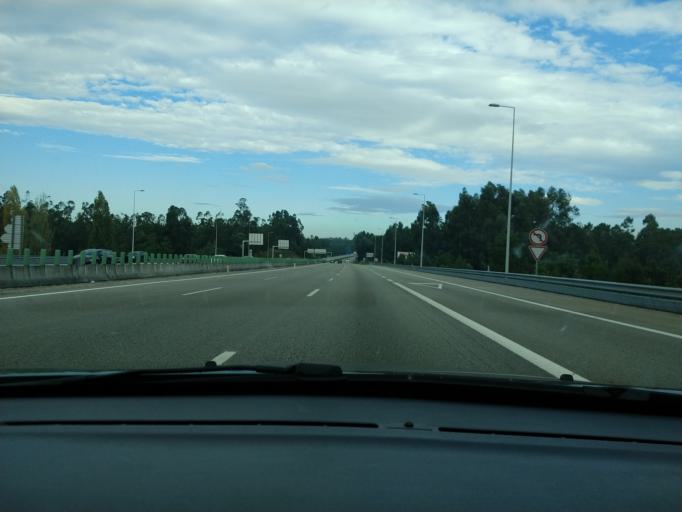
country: PT
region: Aveiro
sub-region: Santa Maria da Feira
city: Feira
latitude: 40.9311
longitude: -8.5699
